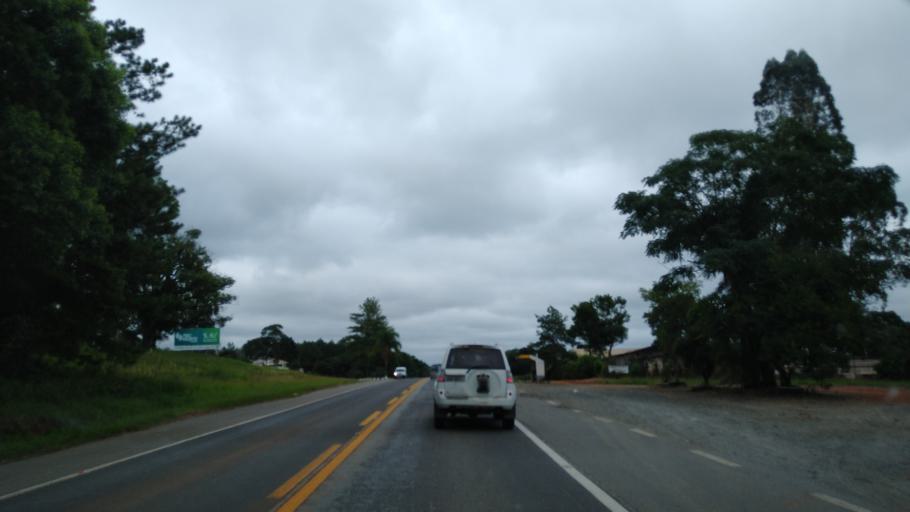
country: BR
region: Santa Catarina
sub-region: Tres Barras
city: Tres Barras
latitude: -26.1777
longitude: -50.1838
